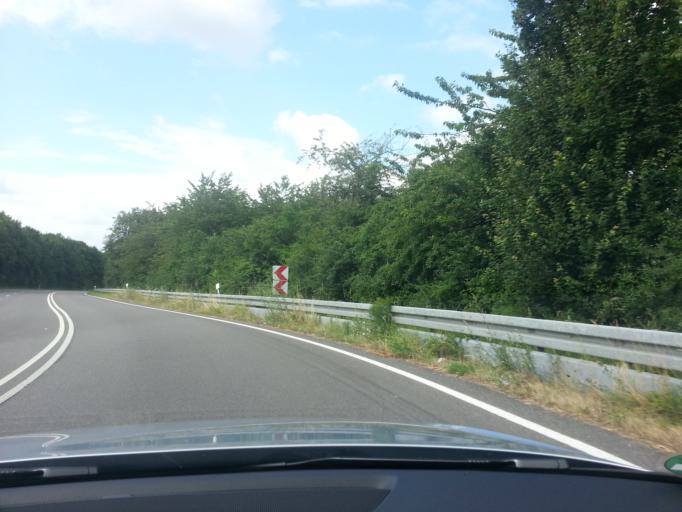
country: DE
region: Rheinland-Pfalz
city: Kirf
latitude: 49.5321
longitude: 6.4370
